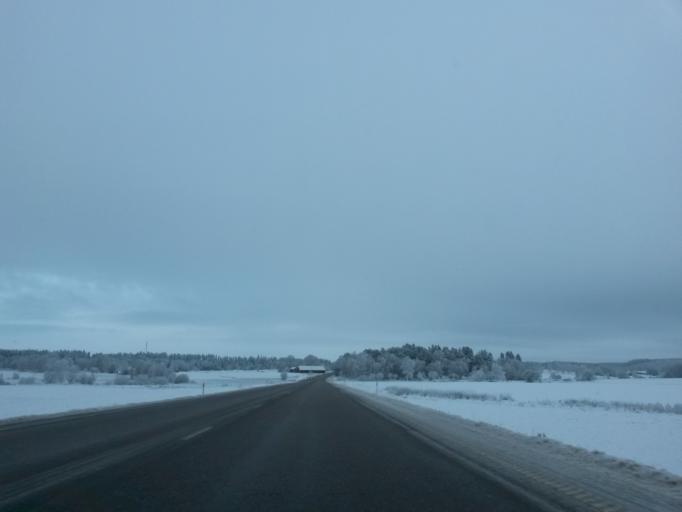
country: SE
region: Vaestra Goetaland
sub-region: Vargarda Kommun
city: Vargarda
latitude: 58.0754
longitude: 12.8149
